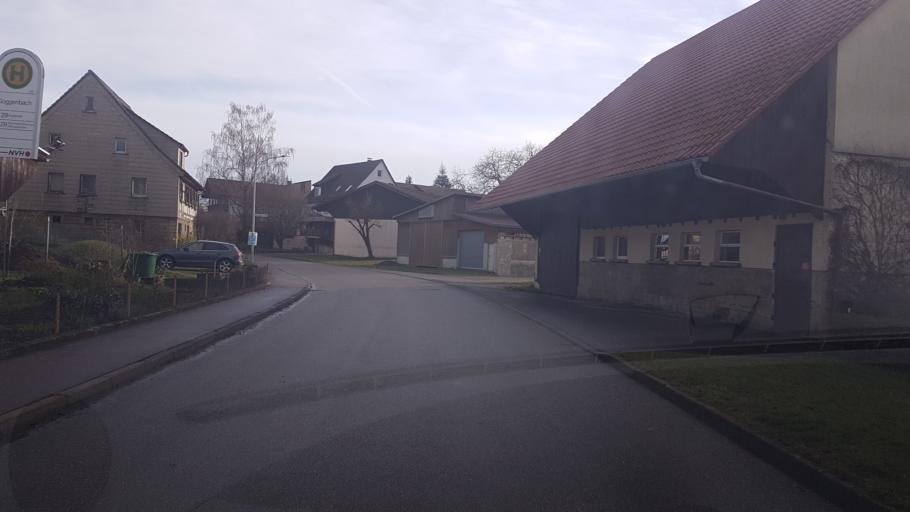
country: DE
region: Baden-Wuerttemberg
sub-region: Regierungsbezirk Stuttgart
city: Kupferzell
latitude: 49.2112
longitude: 9.7302
